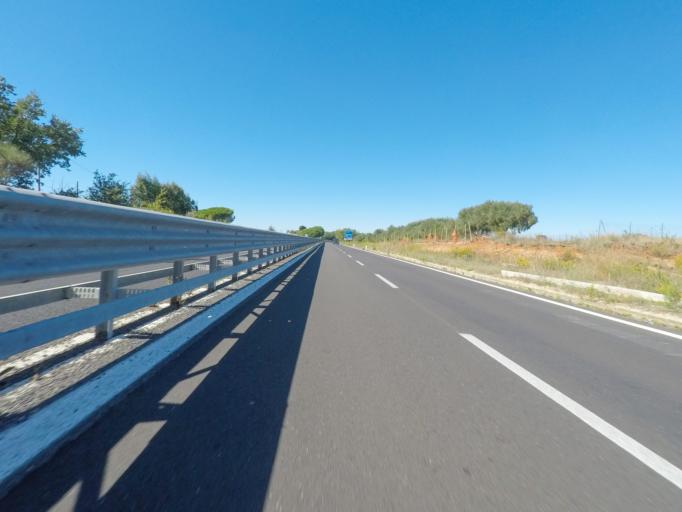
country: IT
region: Latium
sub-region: Provincia di Viterbo
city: Montalto di Castro
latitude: 42.3071
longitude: 11.6594
